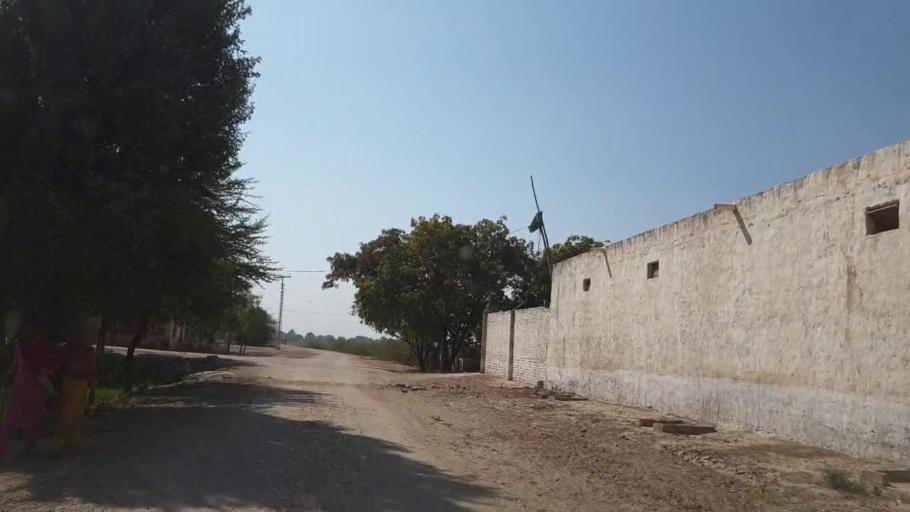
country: PK
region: Sindh
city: Kunri
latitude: 25.1692
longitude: 69.5302
